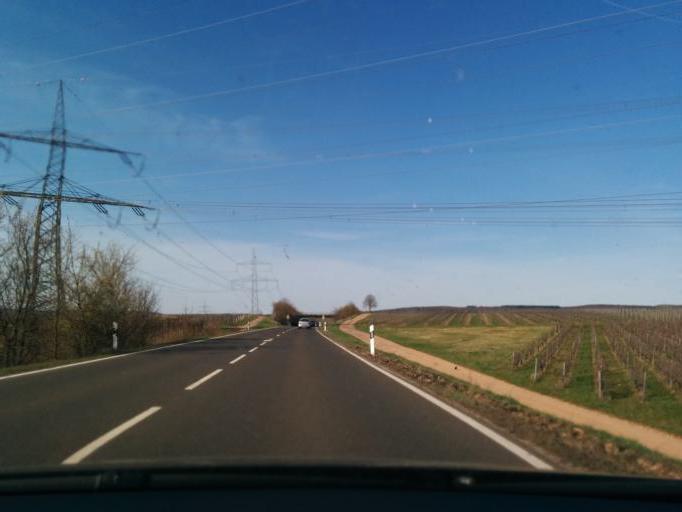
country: DE
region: Rheinland-Pfalz
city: Windesheim
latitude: 49.8912
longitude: 7.8188
